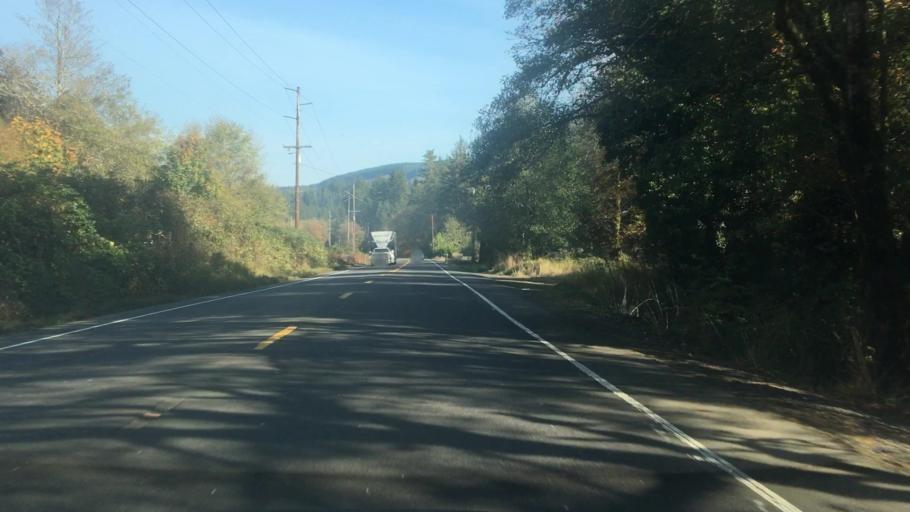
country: US
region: Oregon
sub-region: Lincoln County
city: Rose Lodge
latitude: 45.0223
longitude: -123.8355
